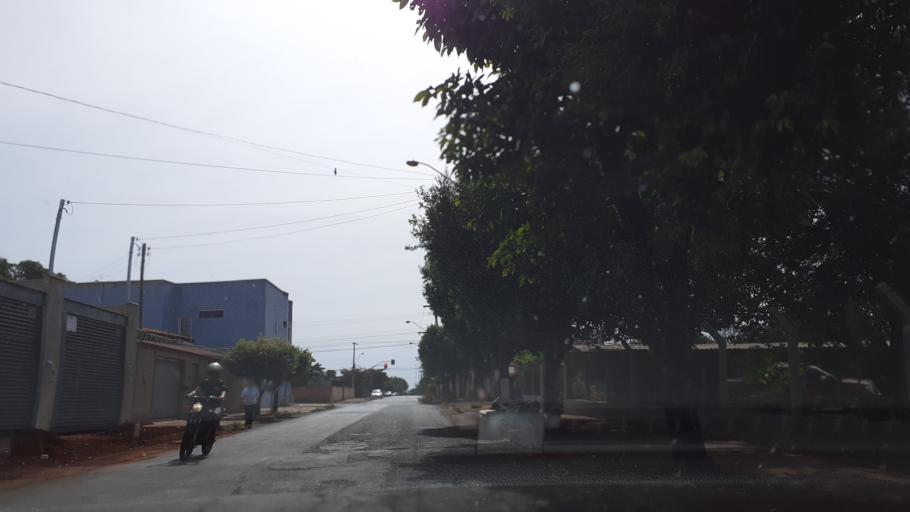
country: BR
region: Goias
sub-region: Itumbiara
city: Itumbiara
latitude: -18.4191
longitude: -49.2324
